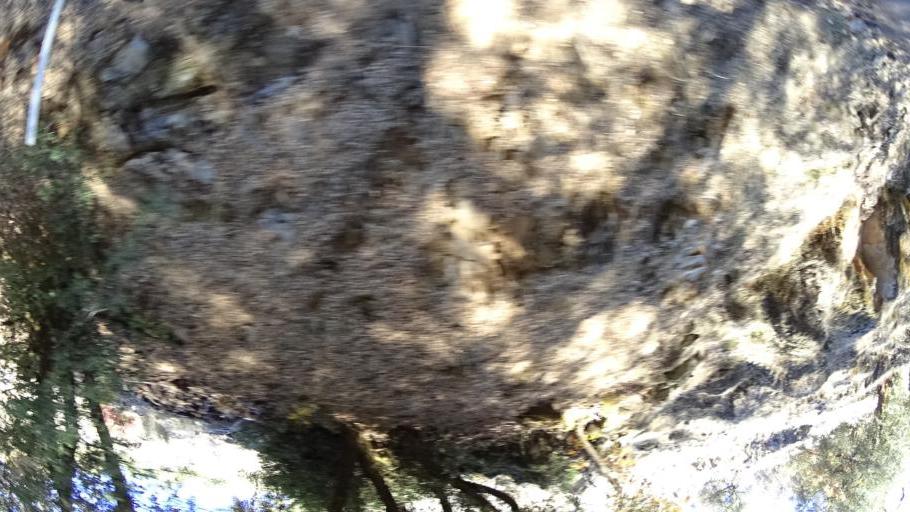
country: US
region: California
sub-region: Siskiyou County
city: Happy Camp
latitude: 41.3019
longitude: -123.1495
